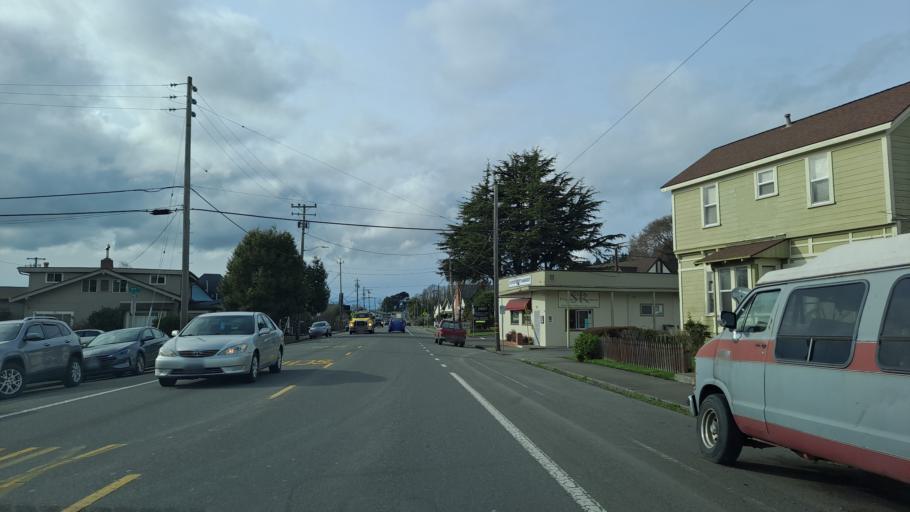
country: US
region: California
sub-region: Humboldt County
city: Fortuna
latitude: 40.5982
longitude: -124.1597
